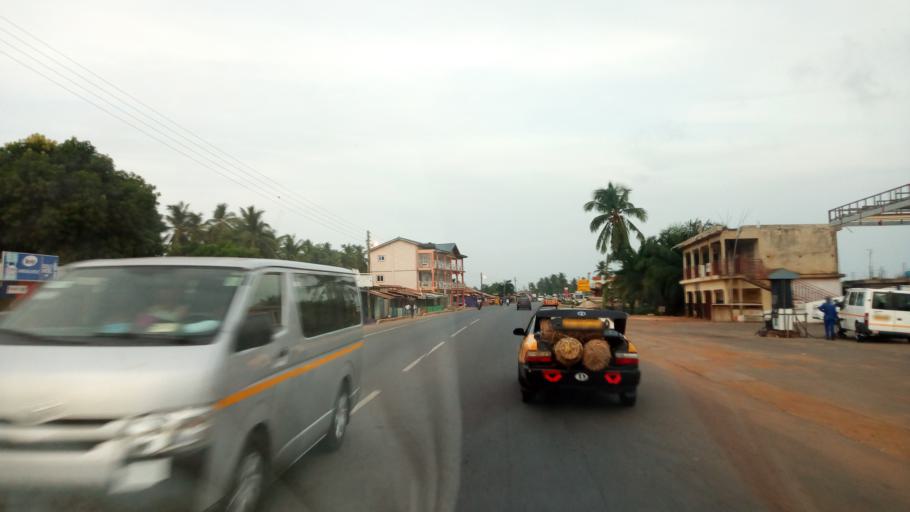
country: TG
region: Maritime
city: Lome
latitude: 6.1188
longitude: 1.1775
